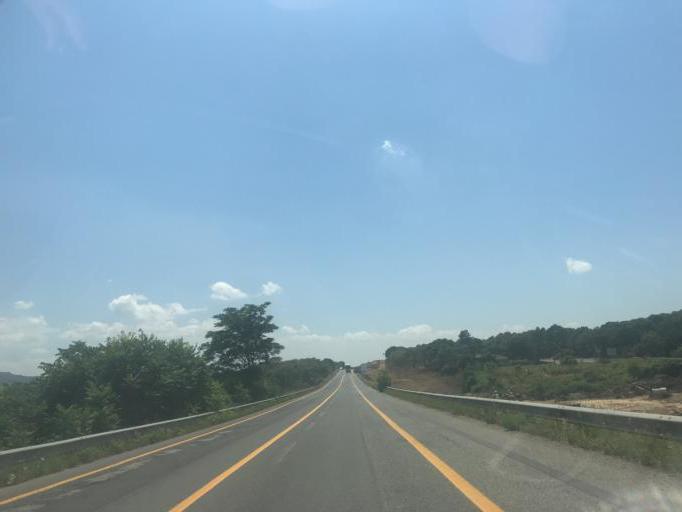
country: IT
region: Sardinia
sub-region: Provincia di Olbia-Tempio
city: Monti
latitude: 40.7962
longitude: 9.2706
